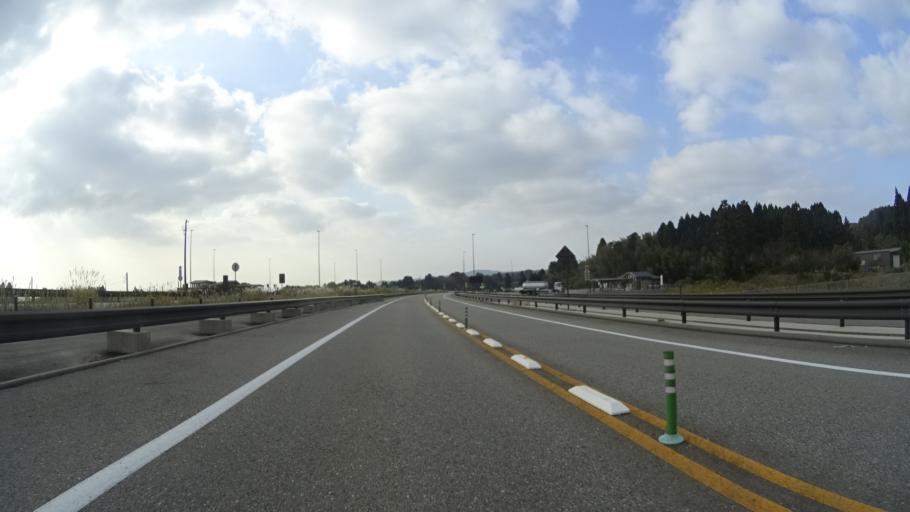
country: JP
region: Ishikawa
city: Nanao
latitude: 36.9629
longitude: 137.0477
